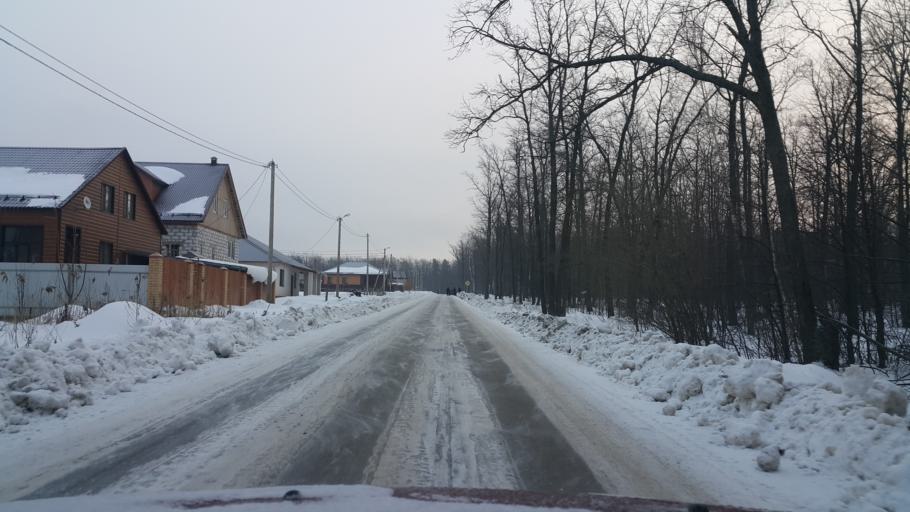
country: RU
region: Tambov
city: Kotovsk
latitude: 52.5717
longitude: 41.5237
